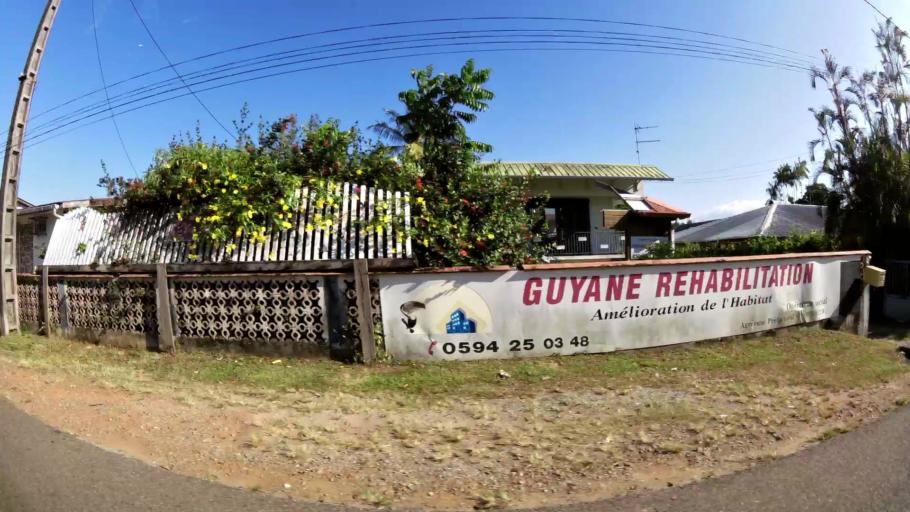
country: GF
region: Guyane
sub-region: Guyane
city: Remire-Montjoly
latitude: 4.8875
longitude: -52.2810
